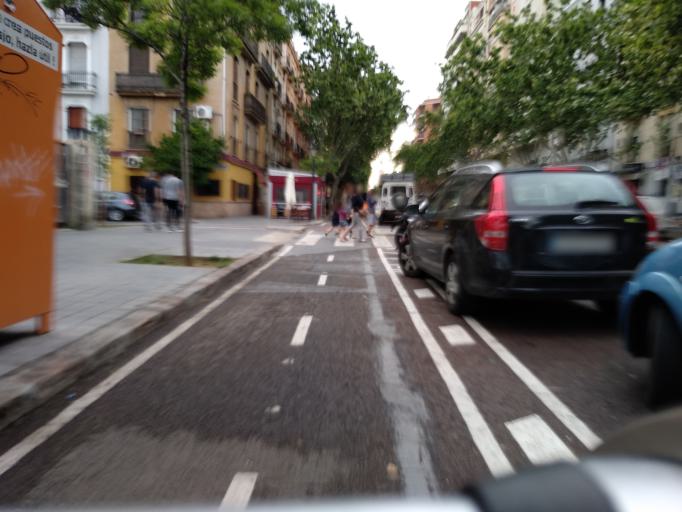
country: ES
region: Valencia
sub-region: Provincia de Valencia
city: Valencia
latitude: 39.4752
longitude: -0.3617
